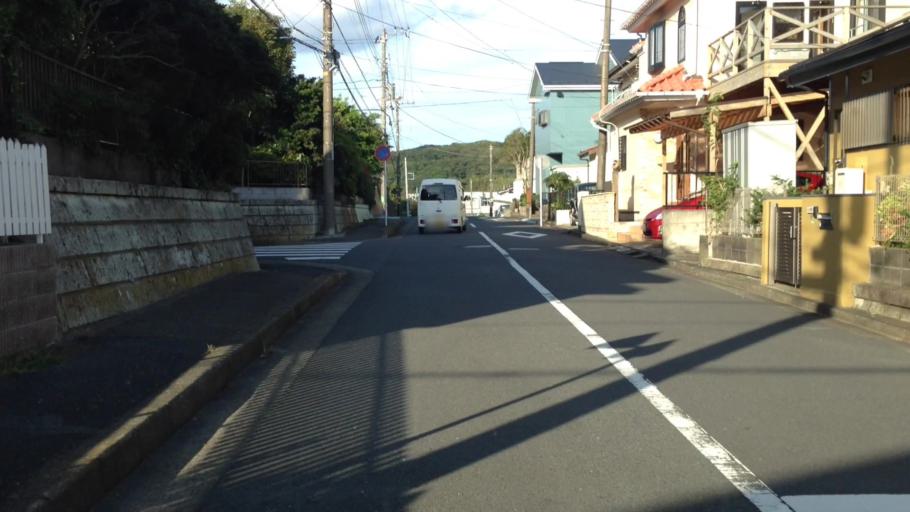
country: JP
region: Kanagawa
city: Yokosuka
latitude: 35.2269
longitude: 139.6267
